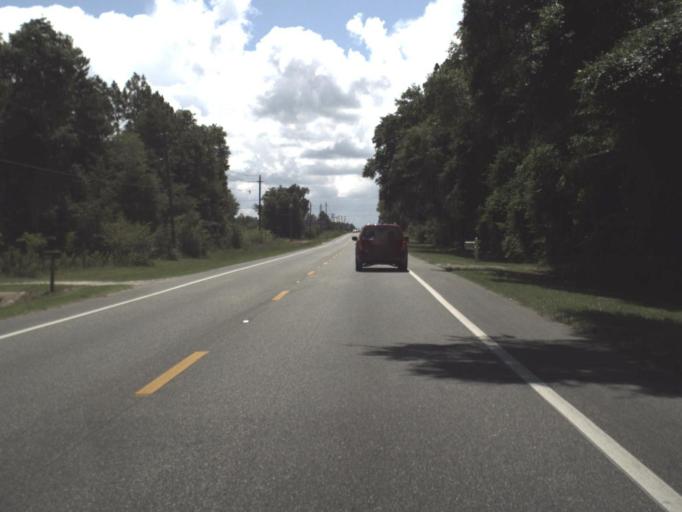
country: US
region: Florida
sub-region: Putnam County
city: Crescent City
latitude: 29.4866
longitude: -81.5706
